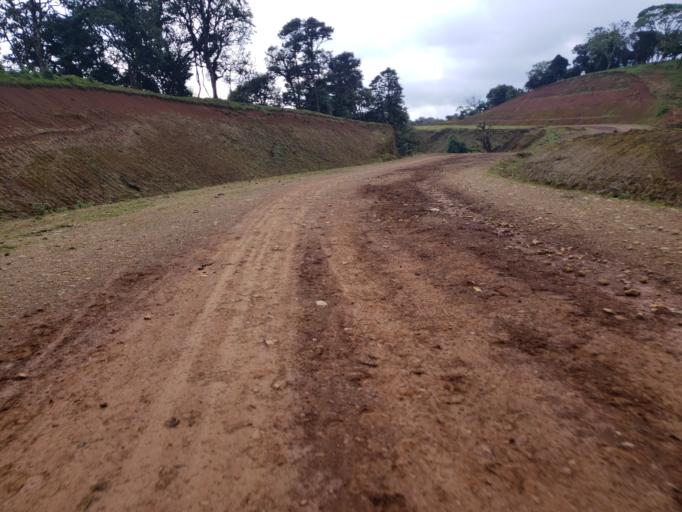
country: ET
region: Oromiya
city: Dodola
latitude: 6.6726
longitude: 39.3644
